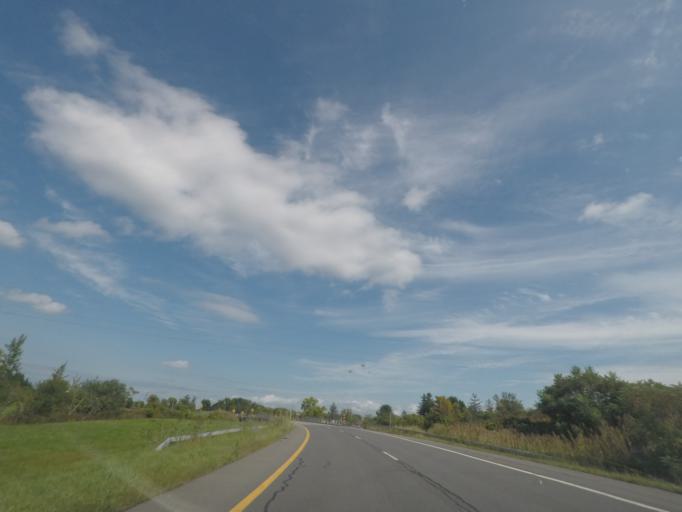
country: US
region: New York
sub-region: Albany County
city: Delmar
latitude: 42.6160
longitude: -73.7864
